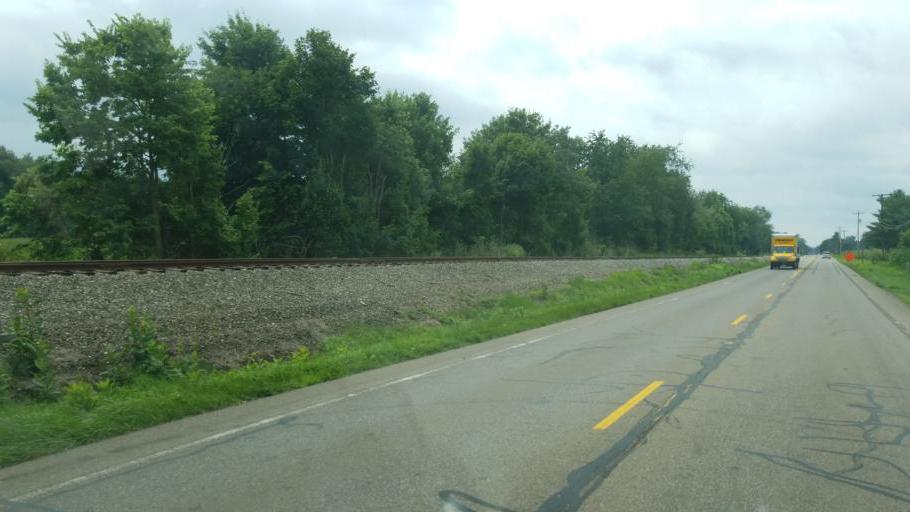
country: US
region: Ohio
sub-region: Licking County
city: Newark
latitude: 40.1457
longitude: -82.4263
